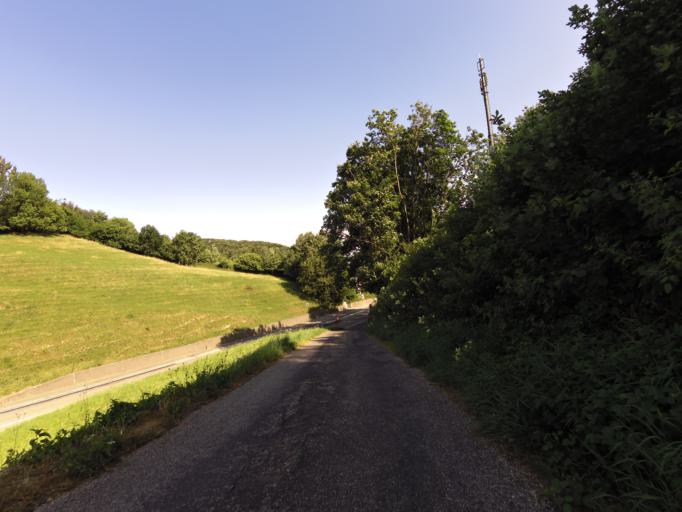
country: CH
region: Basel-Landschaft
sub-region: Bezirk Sissach
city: Laufelfingen
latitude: 47.3818
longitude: 7.8681
